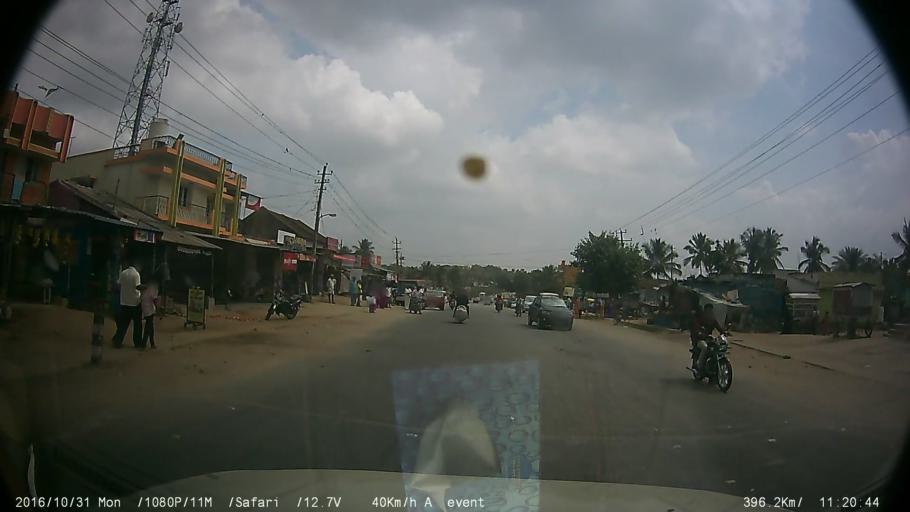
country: IN
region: Karnataka
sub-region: Mysore
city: Piriyapatna
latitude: 12.3368
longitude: 76.1583
